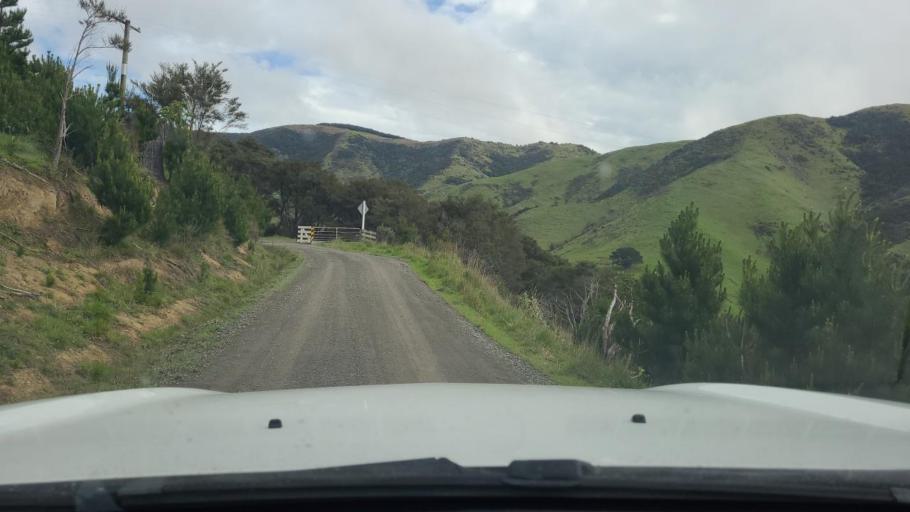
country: NZ
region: Wellington
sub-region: South Wairarapa District
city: Waipawa
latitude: -41.3588
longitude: 175.3928
